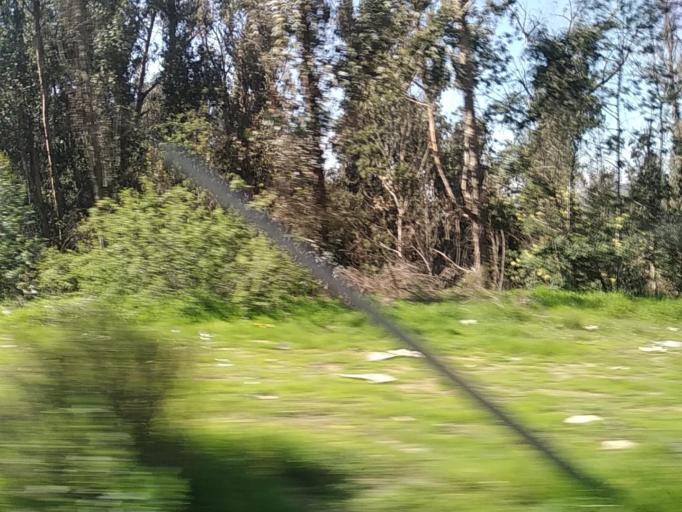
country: CL
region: Valparaiso
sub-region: Provincia de Valparaiso
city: Vina del Mar
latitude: -33.0407
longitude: -71.5064
